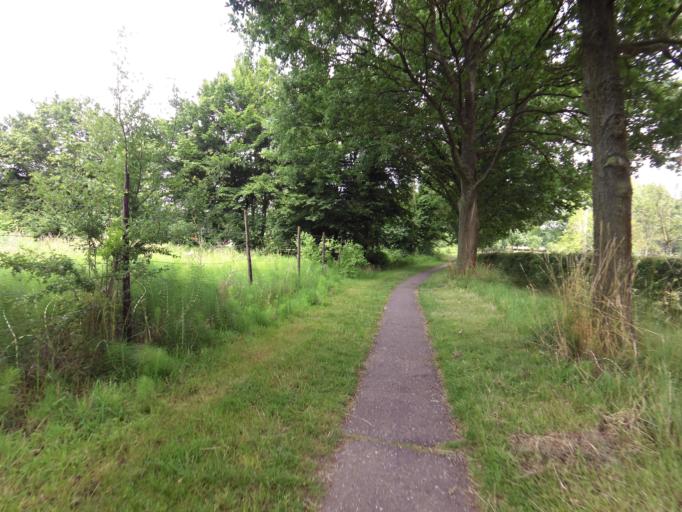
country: NL
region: Limburg
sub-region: Gemeente Voerendaal
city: Voerendaal
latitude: 50.8868
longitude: 5.9250
